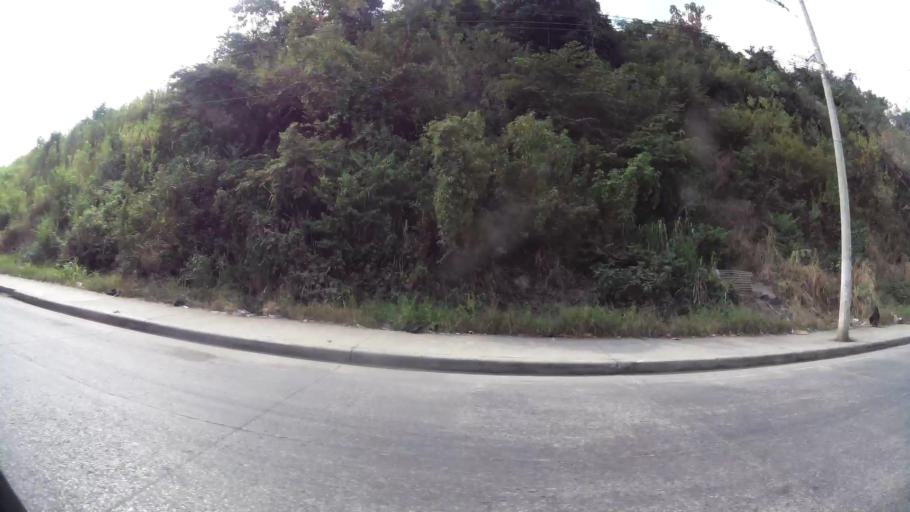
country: EC
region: Guayas
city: Santa Lucia
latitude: -2.1204
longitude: -79.9703
